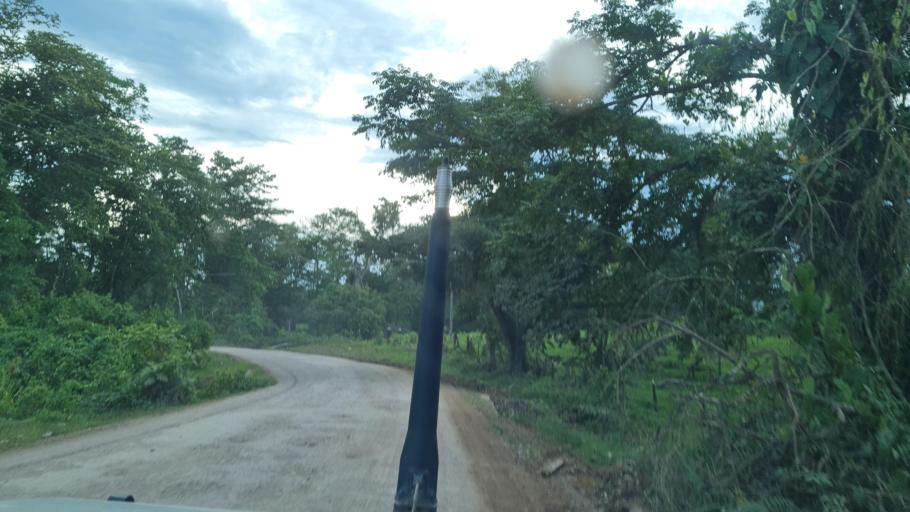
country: NI
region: Atlantico Norte (RAAN)
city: Siuna
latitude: 13.6869
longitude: -84.6115
